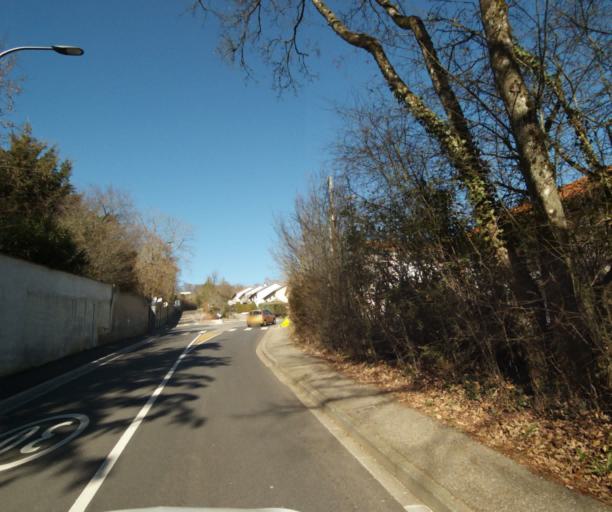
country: FR
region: Lorraine
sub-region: Departement de Meurthe-et-Moselle
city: Saint-Max
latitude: 48.7096
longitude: 6.2152
